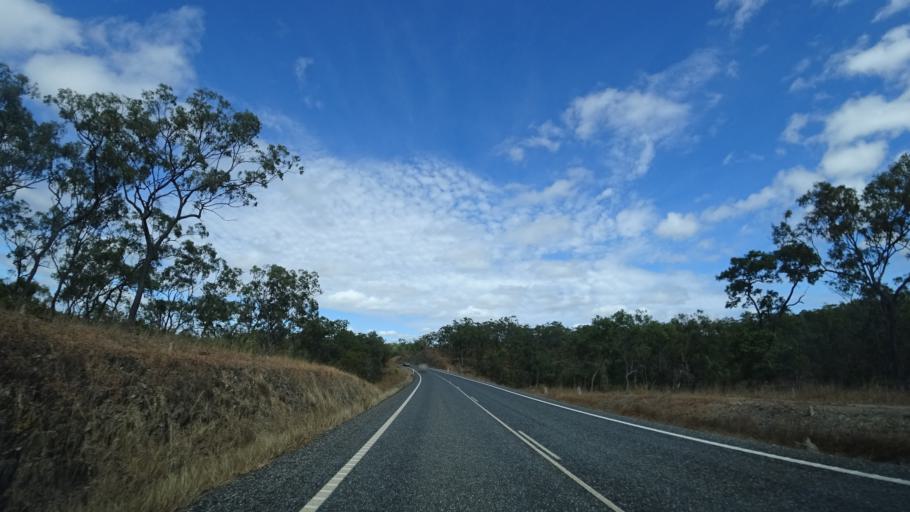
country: AU
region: Queensland
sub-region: Cairns
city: Port Douglas
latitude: -16.2717
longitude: 144.7160
